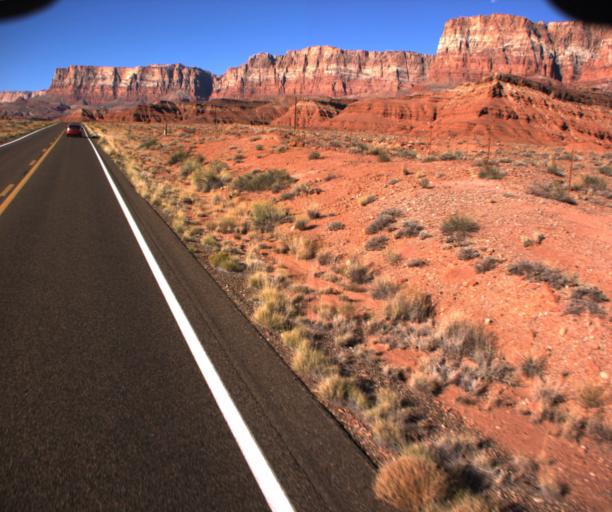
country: US
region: Arizona
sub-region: Coconino County
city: Page
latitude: 36.8109
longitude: -111.6595
